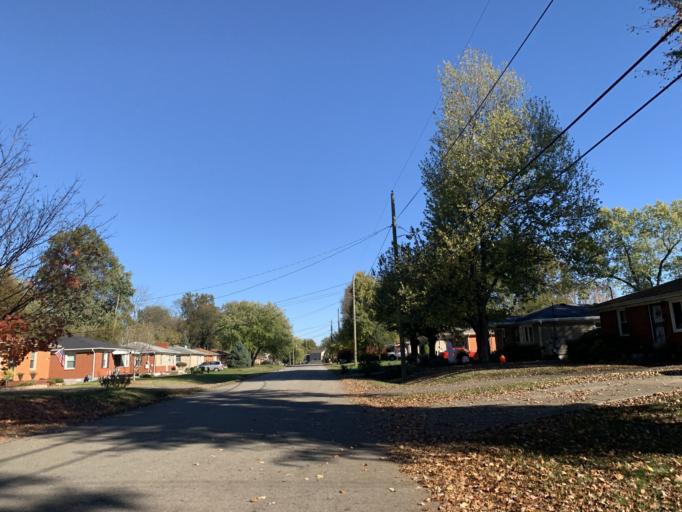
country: US
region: Kentucky
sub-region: Jefferson County
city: Pleasure Ridge Park
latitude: 38.1600
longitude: -85.8664
